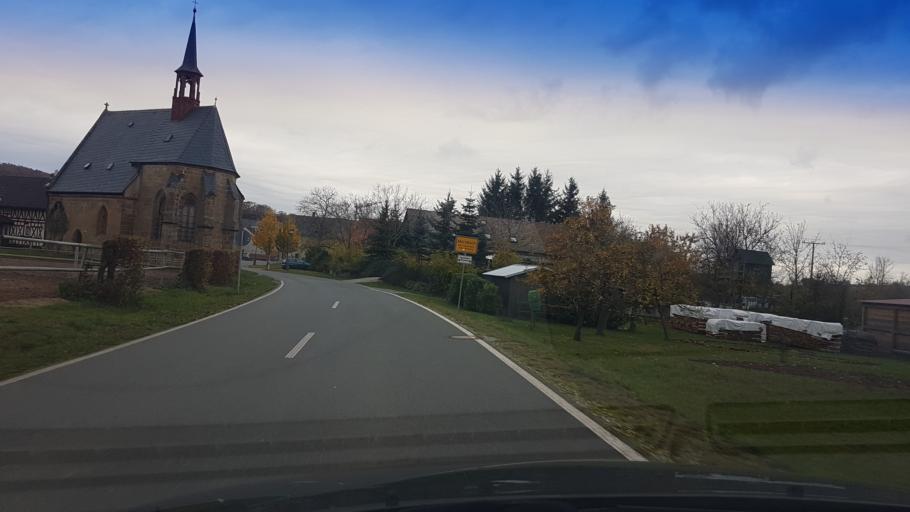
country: DE
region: Bavaria
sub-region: Upper Franconia
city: Rattelsdorf
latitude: 50.0595
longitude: 10.8690
